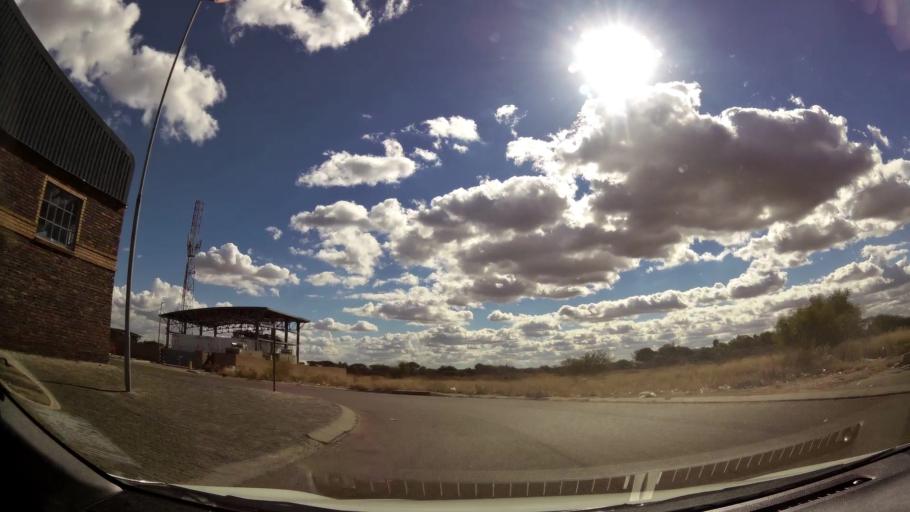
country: ZA
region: Limpopo
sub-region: Capricorn District Municipality
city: Polokwane
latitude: -23.8629
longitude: 29.4784
